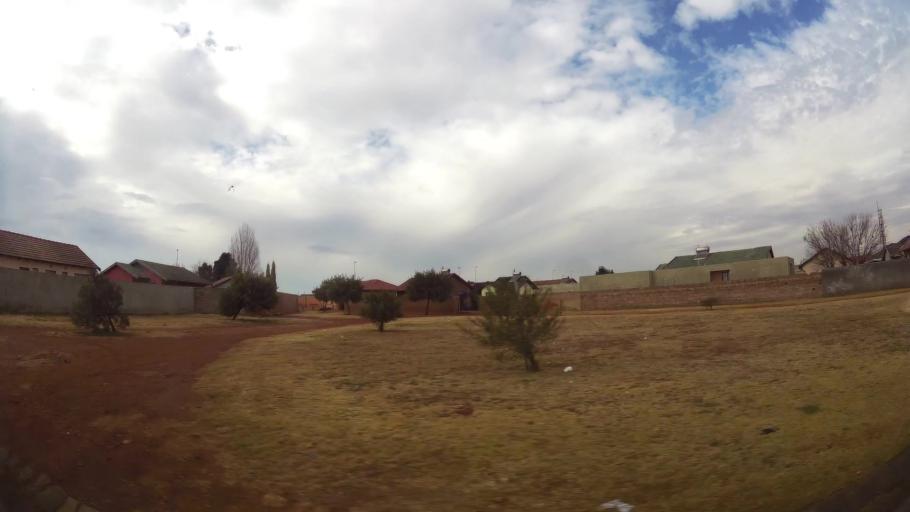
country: ZA
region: Gauteng
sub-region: Ekurhuleni Metropolitan Municipality
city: Germiston
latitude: -26.3303
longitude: 28.1969
